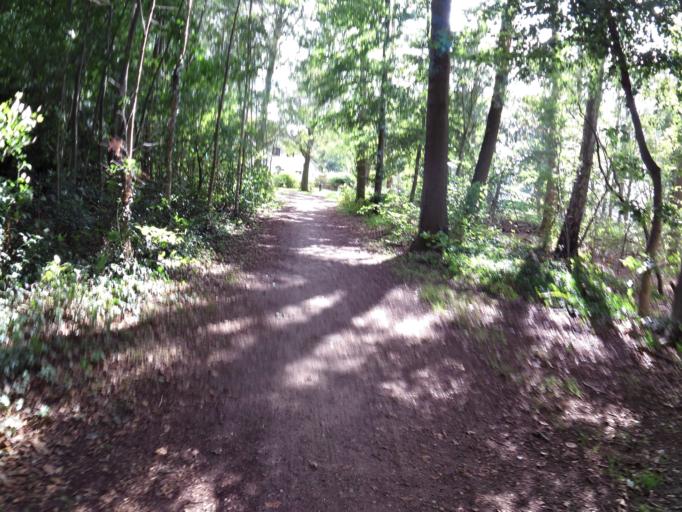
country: NL
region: Gelderland
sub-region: Gemeente Aalten
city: Bredevoort
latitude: 51.9351
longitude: 6.6058
